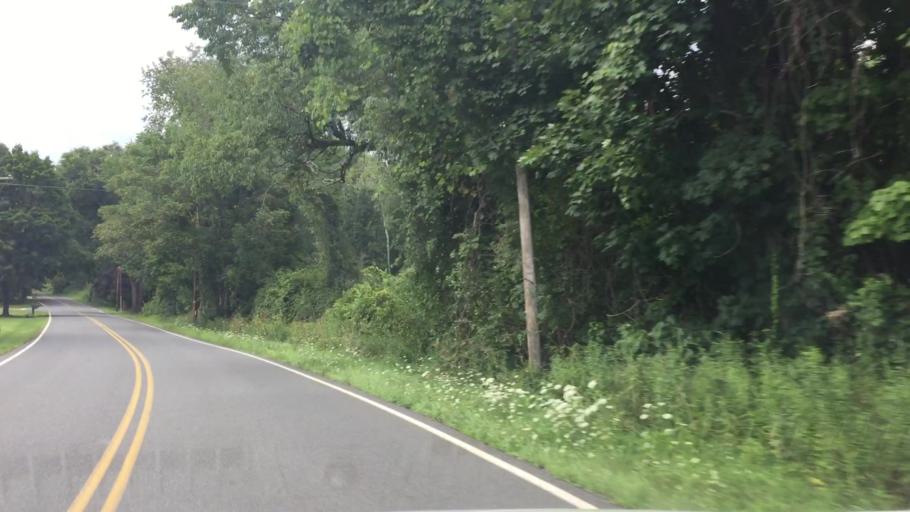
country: US
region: Massachusetts
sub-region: Berkshire County
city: Great Barrington
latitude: 42.2126
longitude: -73.3895
